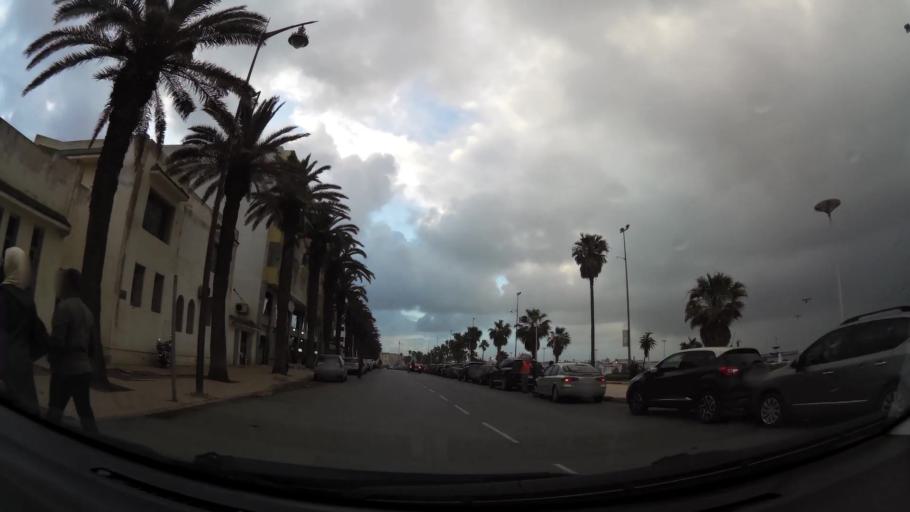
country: MA
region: Doukkala-Abda
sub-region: El-Jadida
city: El Jadida
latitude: 33.2496
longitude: -8.4984
